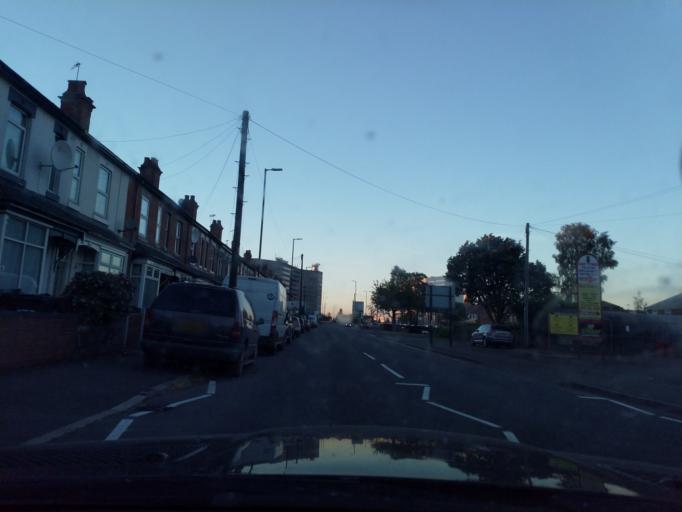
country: GB
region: England
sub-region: City and Borough of Birmingham
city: Acocks Green
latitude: 52.4595
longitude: -1.8179
